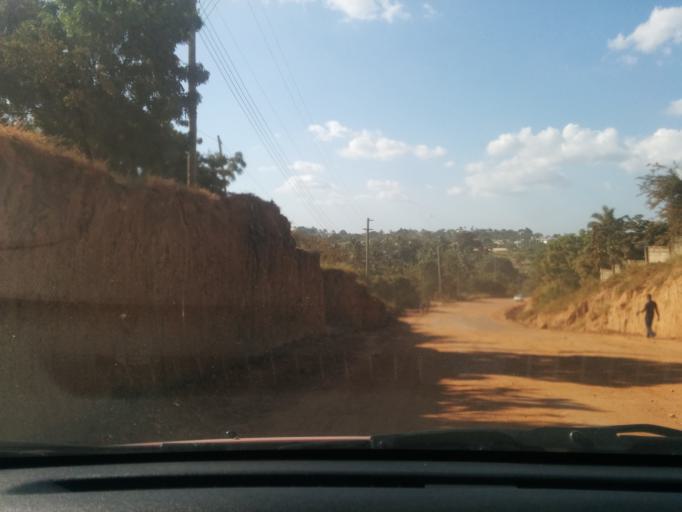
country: TZ
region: Dar es Salaam
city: Magomeni
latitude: -6.7688
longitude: 39.1205
